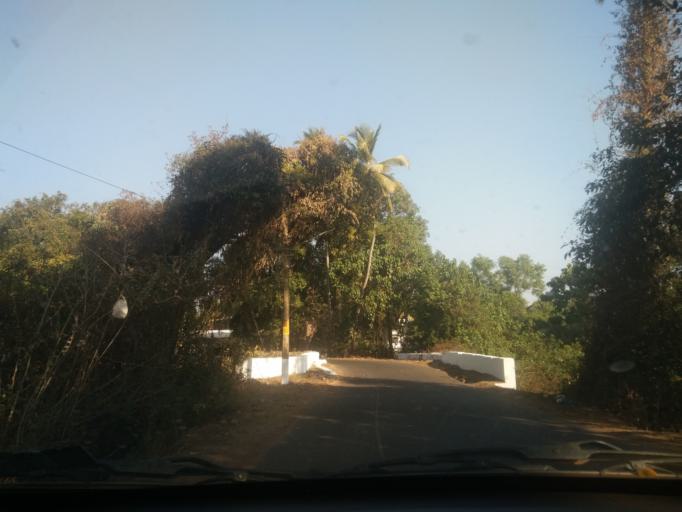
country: IN
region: Goa
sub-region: South Goa
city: Colva
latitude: 15.3051
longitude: 73.9133
